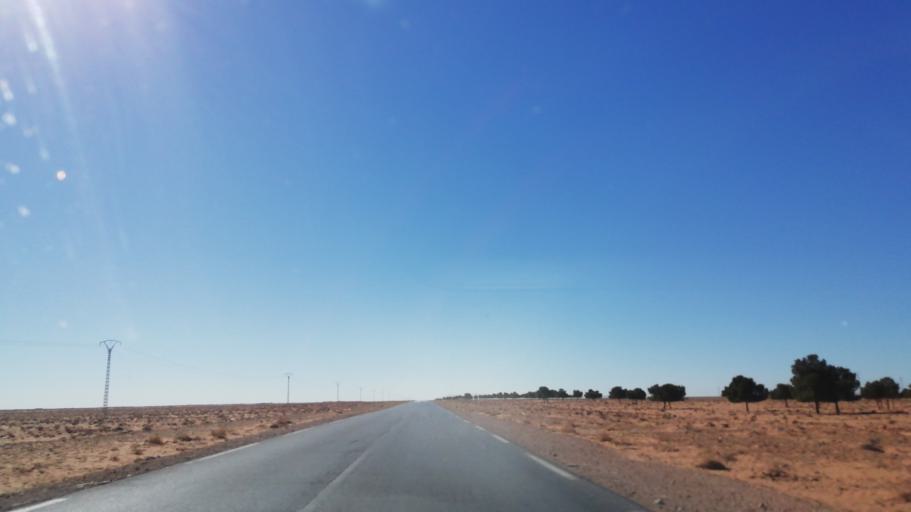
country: DZ
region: Saida
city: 'Ain el Hadjar
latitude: 33.9873
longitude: 0.0332
